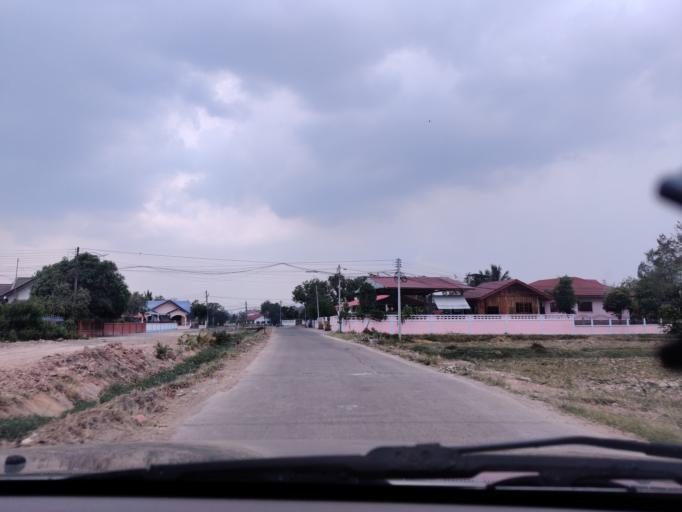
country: TH
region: Sisaket
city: Si Sa Ket
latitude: 15.1073
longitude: 104.3549
